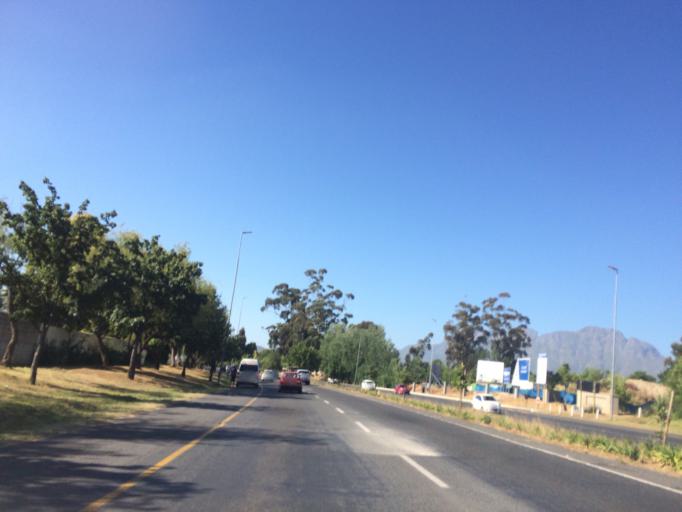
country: ZA
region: Western Cape
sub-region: Cape Winelands District Municipality
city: Stellenbosch
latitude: -33.9554
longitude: 18.8555
